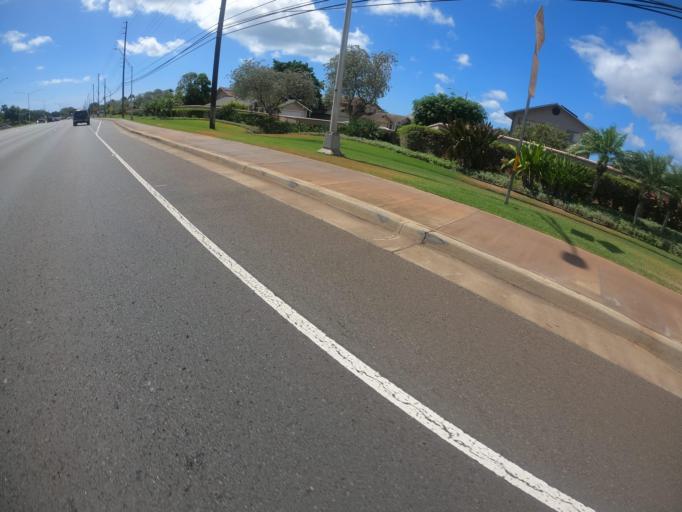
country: US
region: Hawaii
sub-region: Honolulu County
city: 'Ewa Gentry
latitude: 21.3431
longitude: -158.0258
